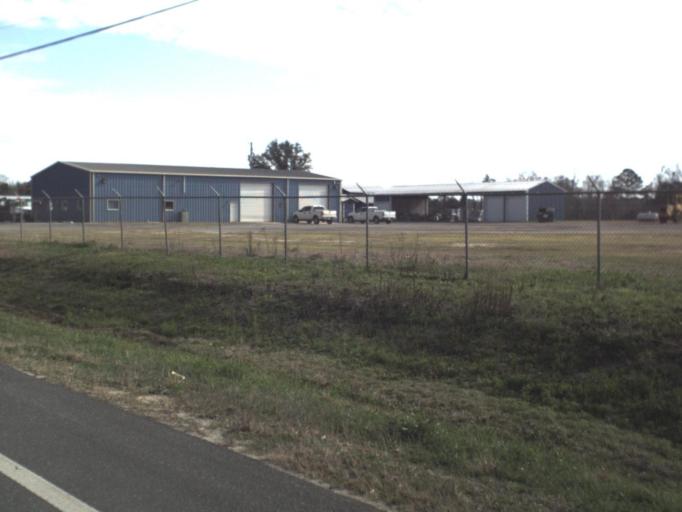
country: US
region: Florida
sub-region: Jackson County
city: Marianna
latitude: 30.8134
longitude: -85.1743
